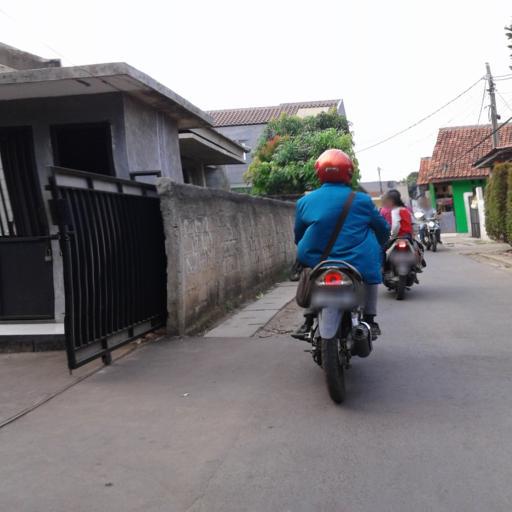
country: ID
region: West Java
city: Sawangan
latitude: -6.3992
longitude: 106.7659
